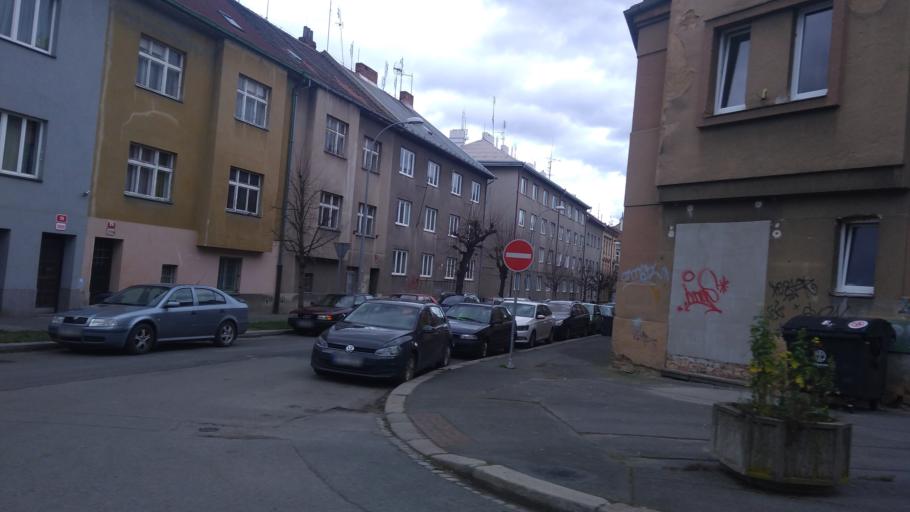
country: CZ
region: Plzensky
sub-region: Okres Plzen-Mesto
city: Pilsen
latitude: 49.7375
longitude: 13.3676
